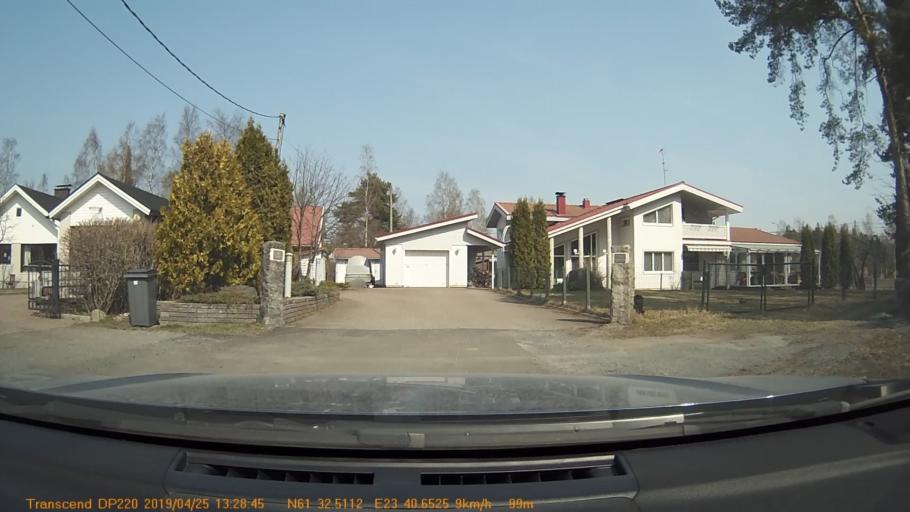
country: FI
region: Pirkanmaa
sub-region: Tampere
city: Yloejaervi
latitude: 61.5418
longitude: 23.6775
